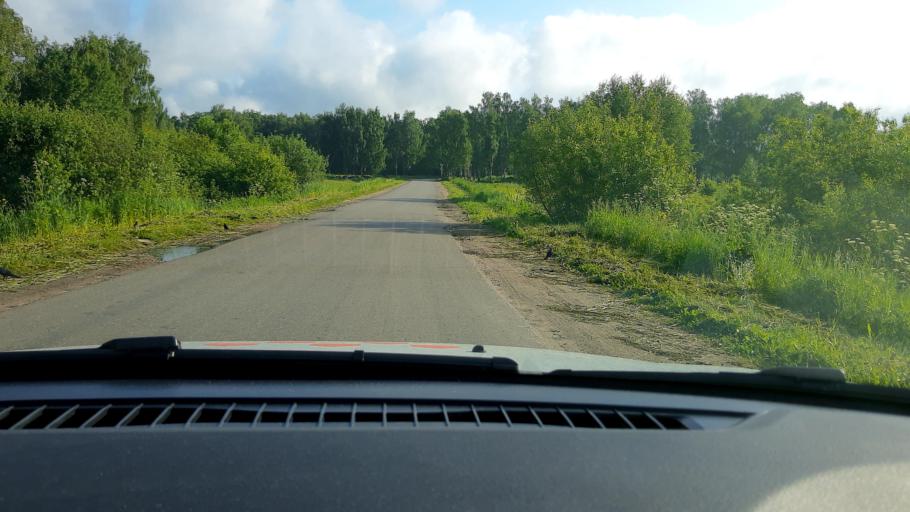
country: RU
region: Nizjnij Novgorod
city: Burevestnik
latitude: 56.1205
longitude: 43.8890
